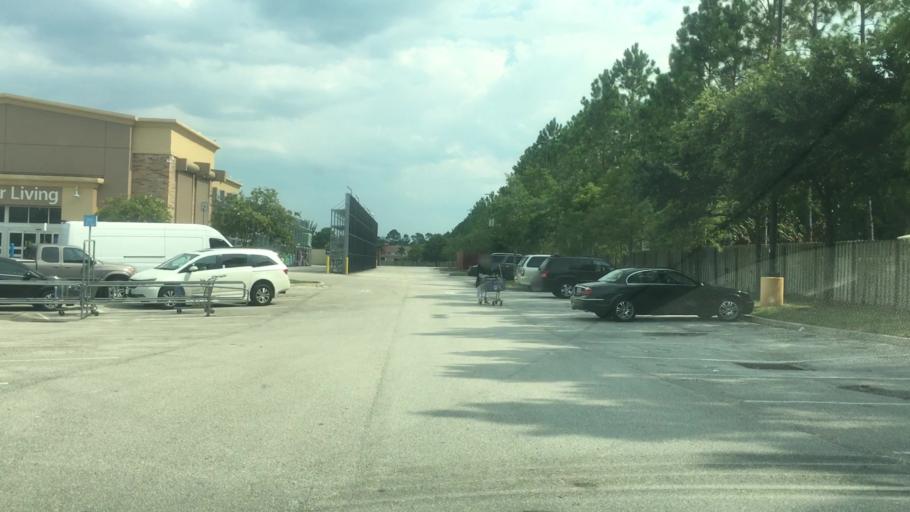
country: US
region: Florida
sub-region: Duval County
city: Jacksonville Beach
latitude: 30.2859
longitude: -81.4639
